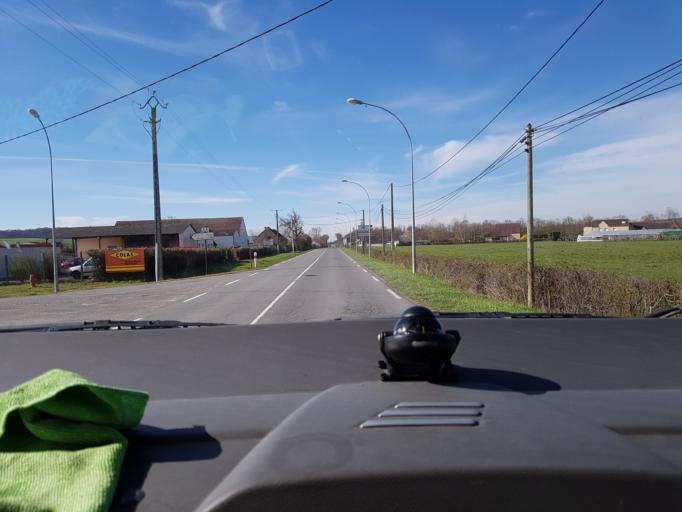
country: FR
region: Bourgogne
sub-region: Departement de Saone-et-Loire
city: Gueugnon
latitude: 46.5723
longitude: 4.0579
